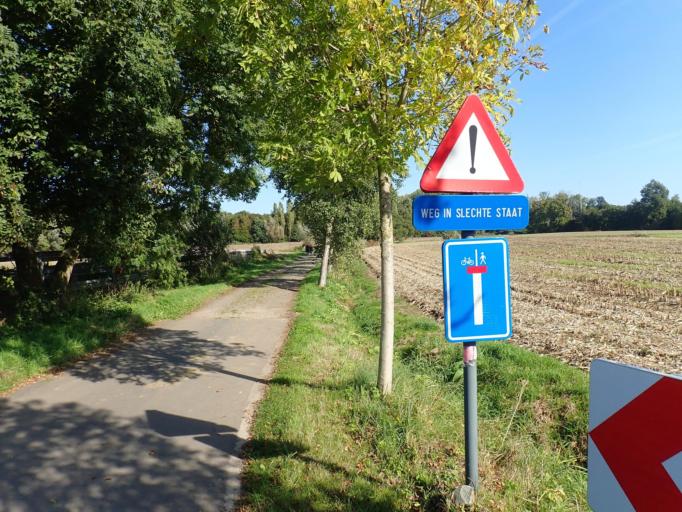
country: BE
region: Flanders
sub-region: Provincie Oost-Vlaanderen
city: Waasmunster
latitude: 51.1152
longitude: 4.0581
